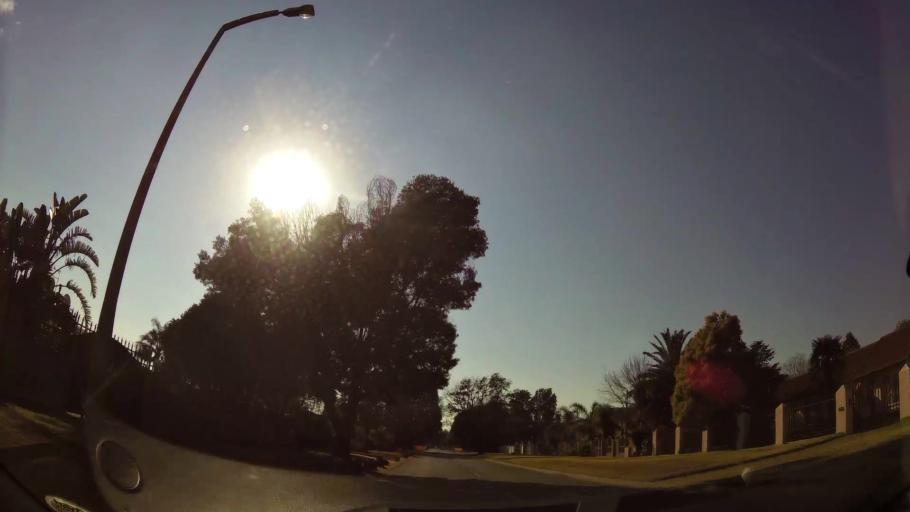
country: ZA
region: Gauteng
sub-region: Ekurhuleni Metropolitan Municipality
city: Benoni
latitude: -26.1484
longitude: 28.3120
